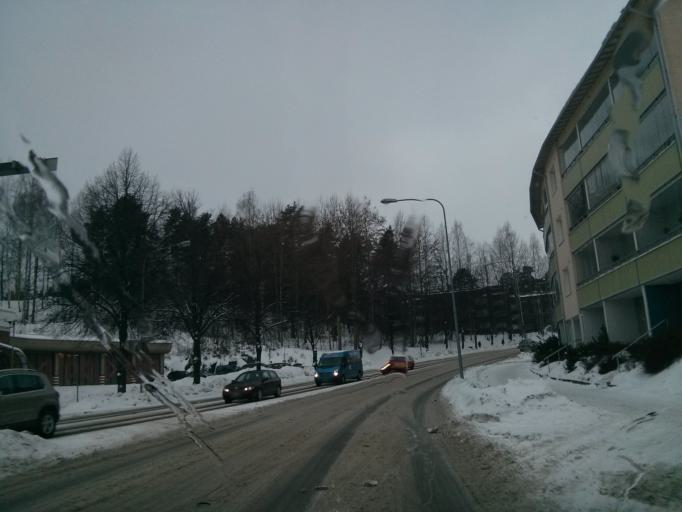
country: FI
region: Southern Savonia
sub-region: Savonlinna
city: Savonlinna
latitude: 61.8683
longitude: 28.8660
